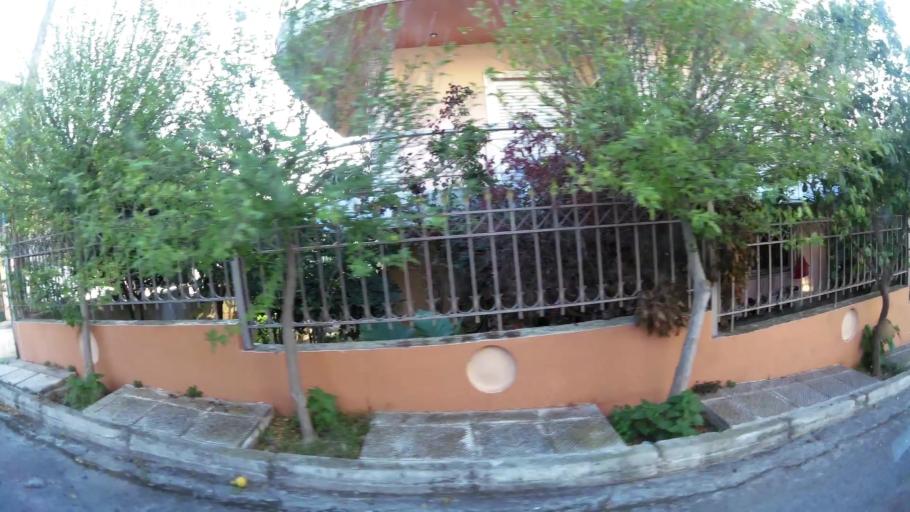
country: GR
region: Attica
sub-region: Nomarchia Dytikis Attikis
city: Zefyri
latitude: 38.0547
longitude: 23.7178
